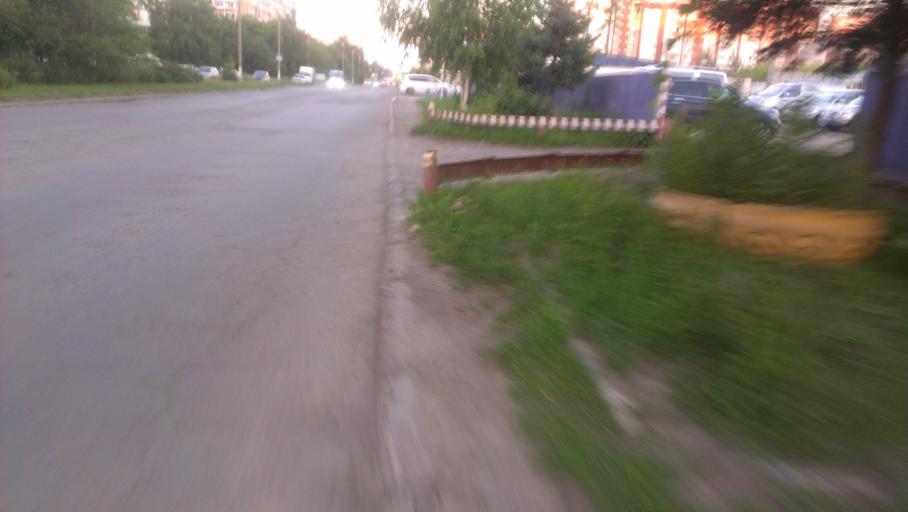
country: RU
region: Altai Krai
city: Novosilikatnyy
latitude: 53.3632
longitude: 83.6623
